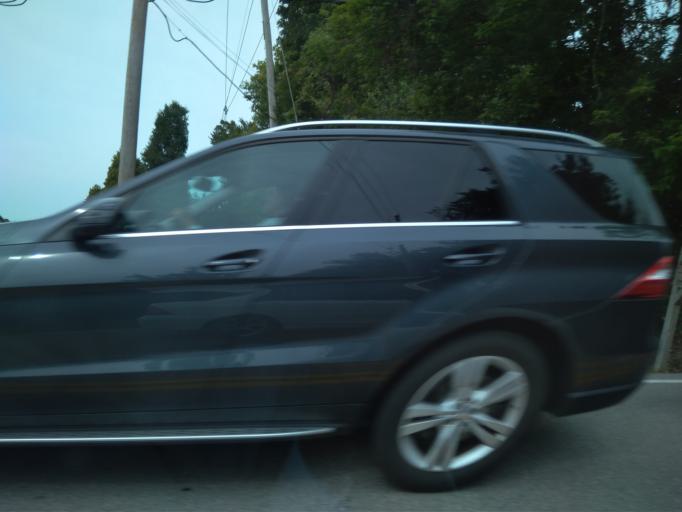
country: US
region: Kentucky
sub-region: Oldham County
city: Pewee Valley
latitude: 38.2865
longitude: -85.4995
